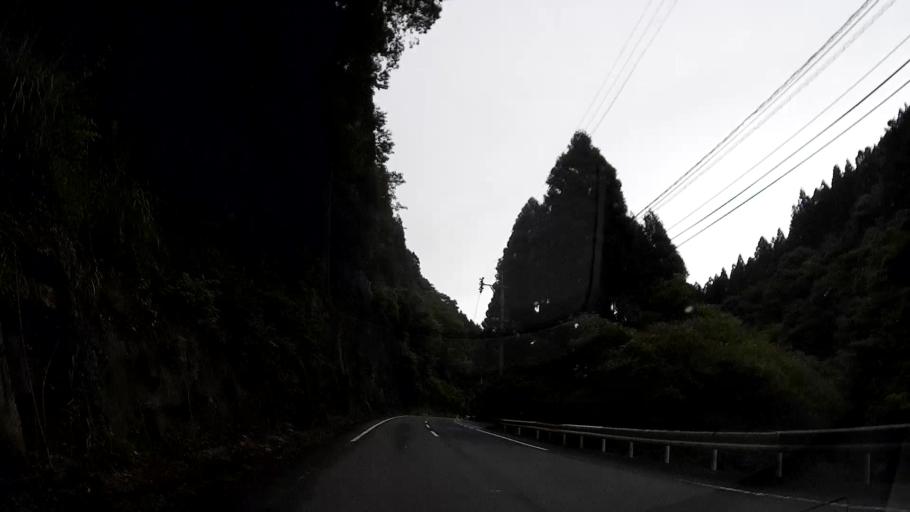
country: JP
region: Kumamoto
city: Kikuchi
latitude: 33.0798
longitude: 130.9361
